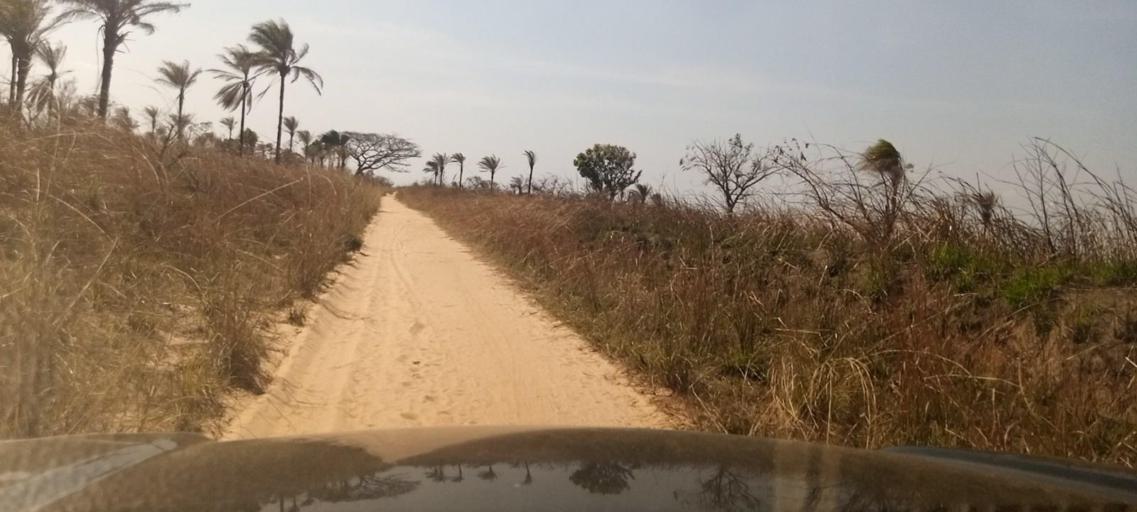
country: CD
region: Kasai-Oriental
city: Kabinda
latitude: -5.7998
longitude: 25.0294
